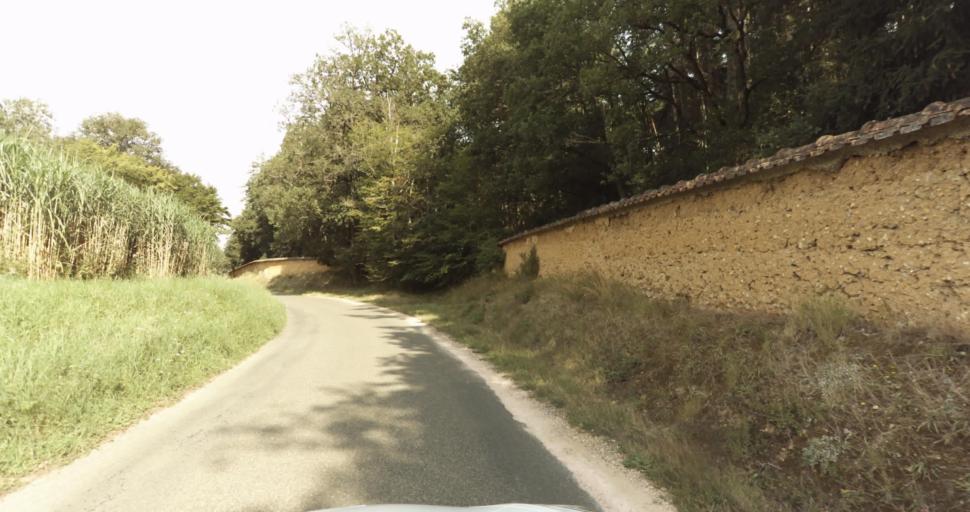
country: FR
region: Haute-Normandie
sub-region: Departement de l'Eure
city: Tillieres-sur-Avre
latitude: 48.7680
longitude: 1.0961
